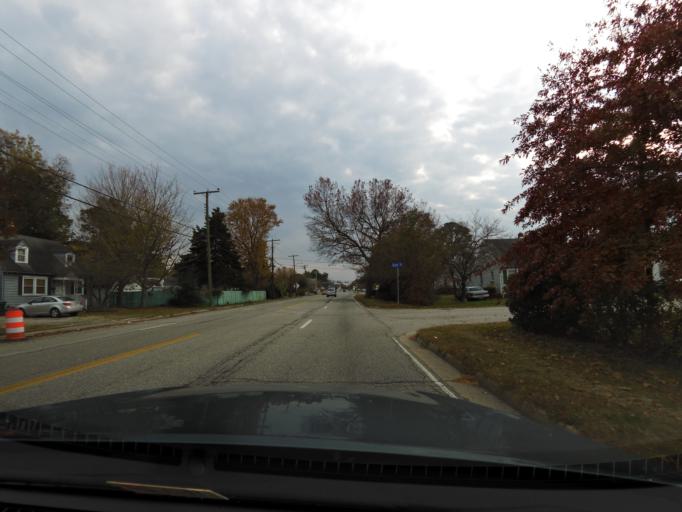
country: US
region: Virginia
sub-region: City of Hampton
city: Hampton
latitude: 37.0150
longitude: -76.3530
